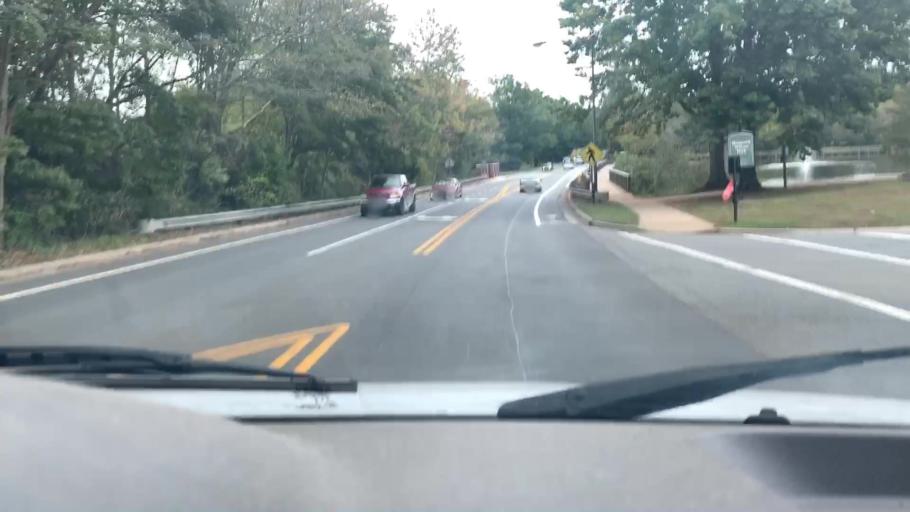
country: US
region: North Carolina
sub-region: Mecklenburg County
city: Cornelius
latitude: 35.5029
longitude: -80.8564
